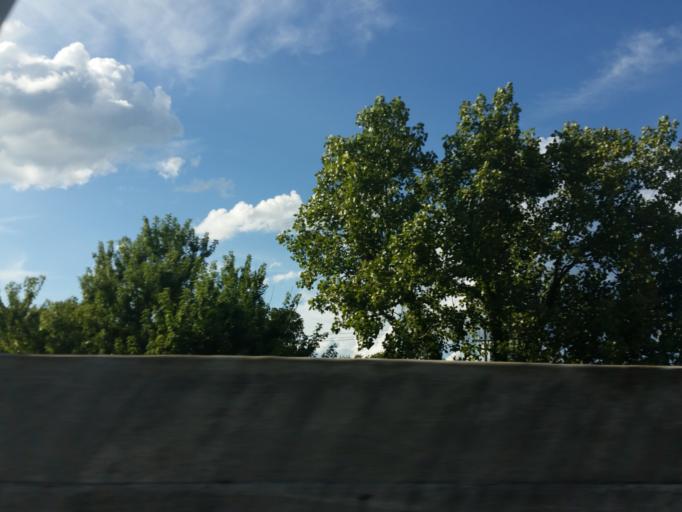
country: US
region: Tennessee
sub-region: Davidson County
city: Nashville
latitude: 36.2403
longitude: -86.7690
